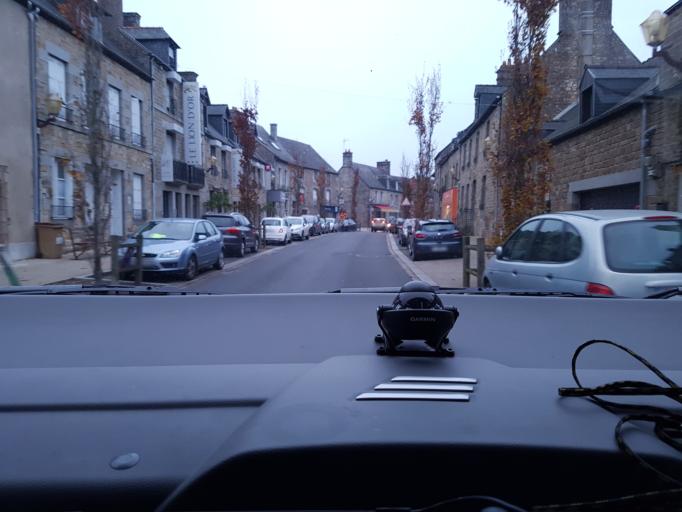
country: FR
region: Brittany
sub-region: Departement d'Ille-et-Vilaine
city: Saint-Brice-en-Cogles
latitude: 48.4111
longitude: -1.3675
